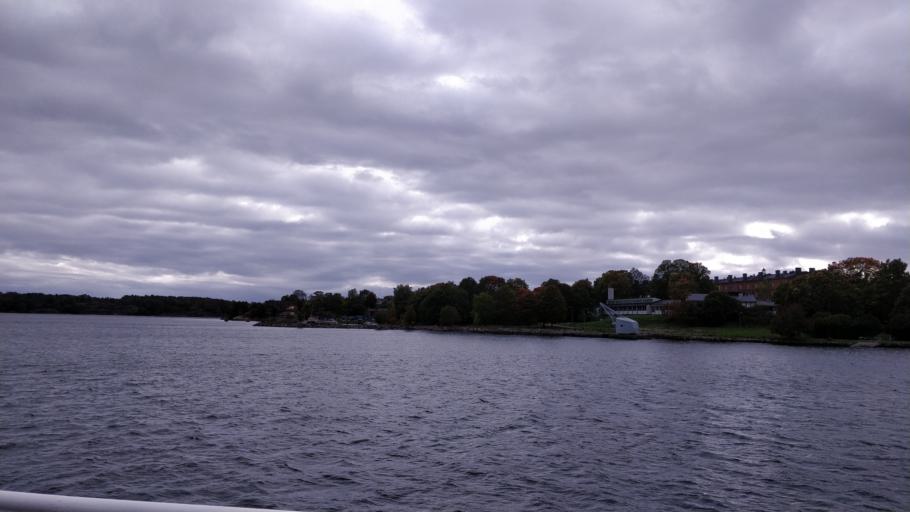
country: FI
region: Uusimaa
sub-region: Helsinki
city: Helsinki
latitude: 60.1506
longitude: 24.9913
